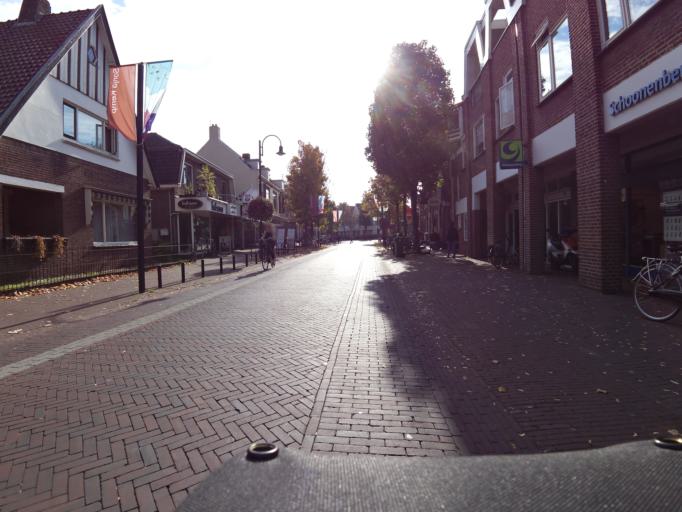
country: NL
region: Gelderland
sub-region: Gemeente Ede
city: Bennekom
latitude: 51.9993
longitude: 5.6760
